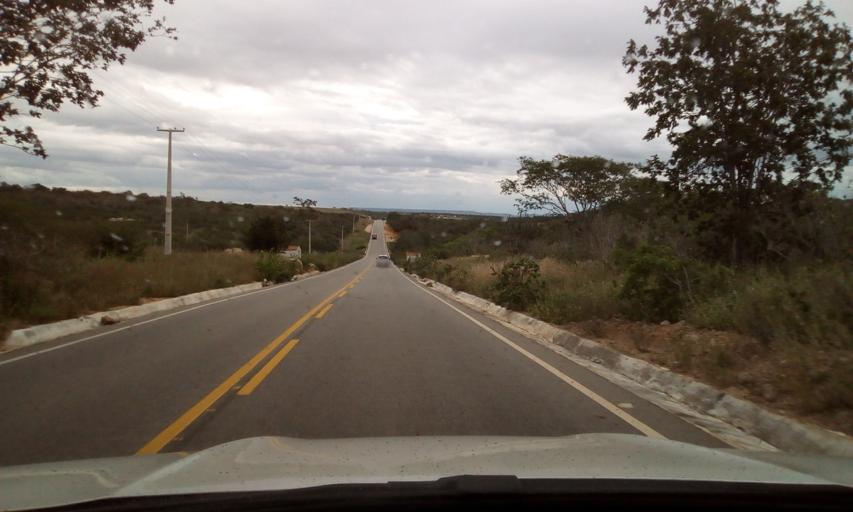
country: BR
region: Paraiba
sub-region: Picui
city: Picui
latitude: -6.5645
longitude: -36.2786
